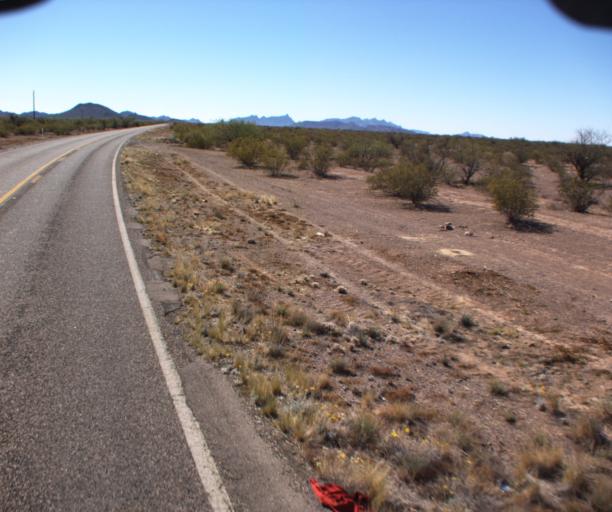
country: US
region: Arizona
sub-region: Pima County
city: Ajo
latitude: 32.3231
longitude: -112.7720
